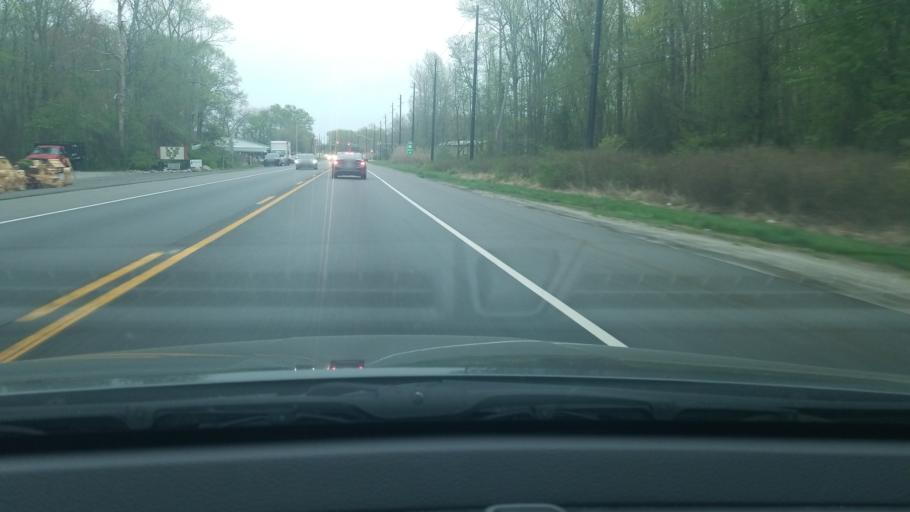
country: US
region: New Jersey
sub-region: Burlington County
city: Leisuretowne
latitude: 39.8886
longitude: -74.7523
